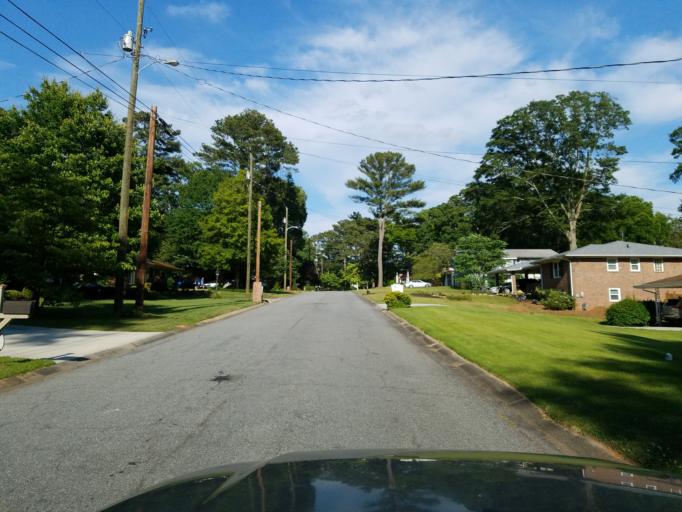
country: US
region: Georgia
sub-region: Cobb County
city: Smyrna
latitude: 33.9331
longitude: -84.4835
